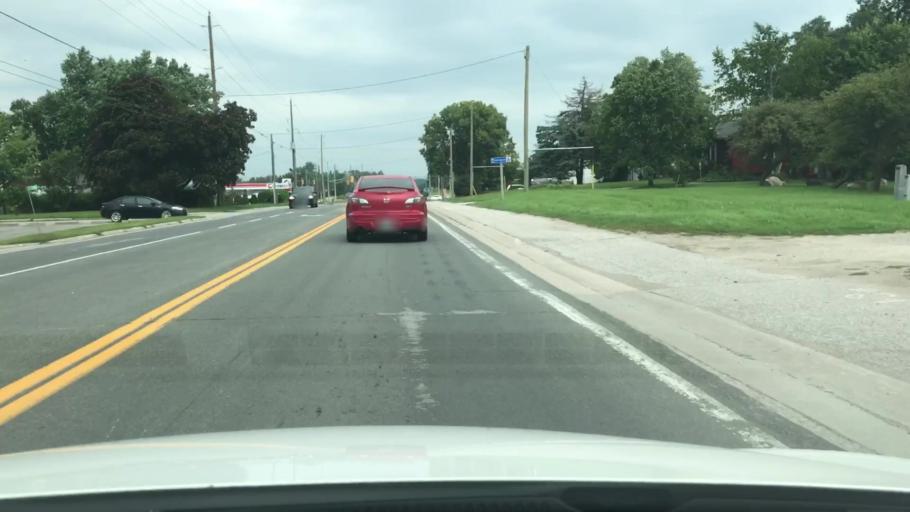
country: CA
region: Ontario
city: Innisfil
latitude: 44.2980
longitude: -79.6129
